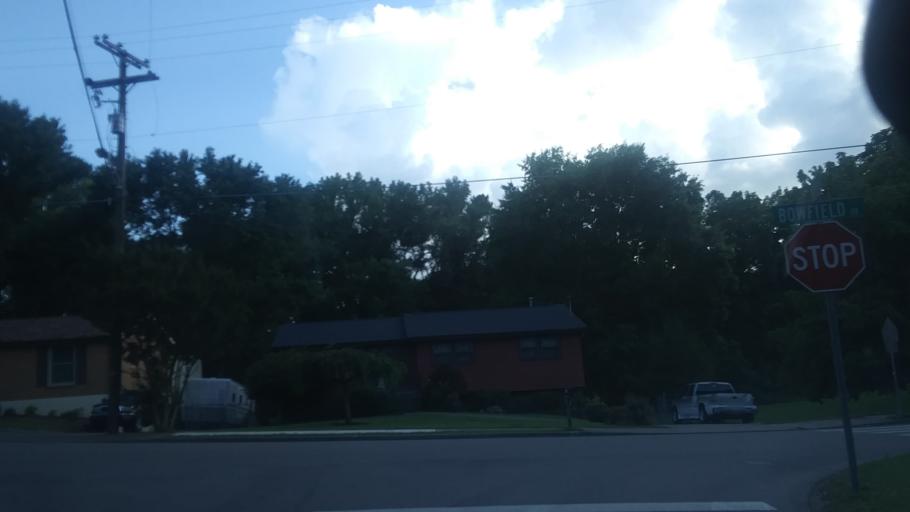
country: US
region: Tennessee
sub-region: Rutherford County
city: La Vergne
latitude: 36.0664
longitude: -86.6682
